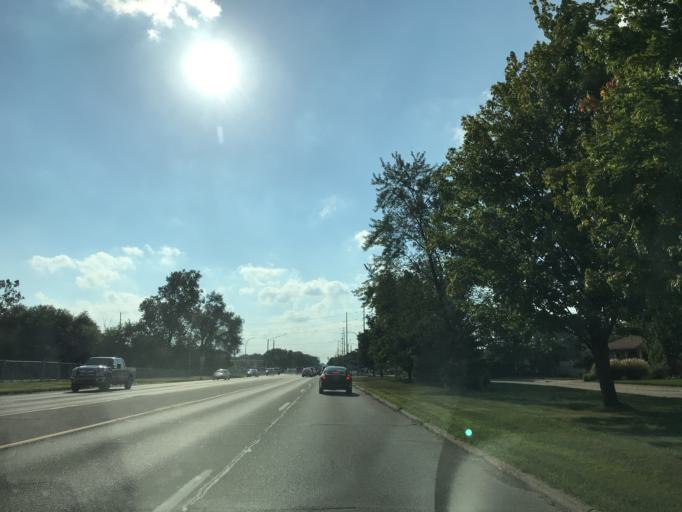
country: US
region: Michigan
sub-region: Wayne County
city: Livonia
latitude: 42.3965
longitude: -83.4100
